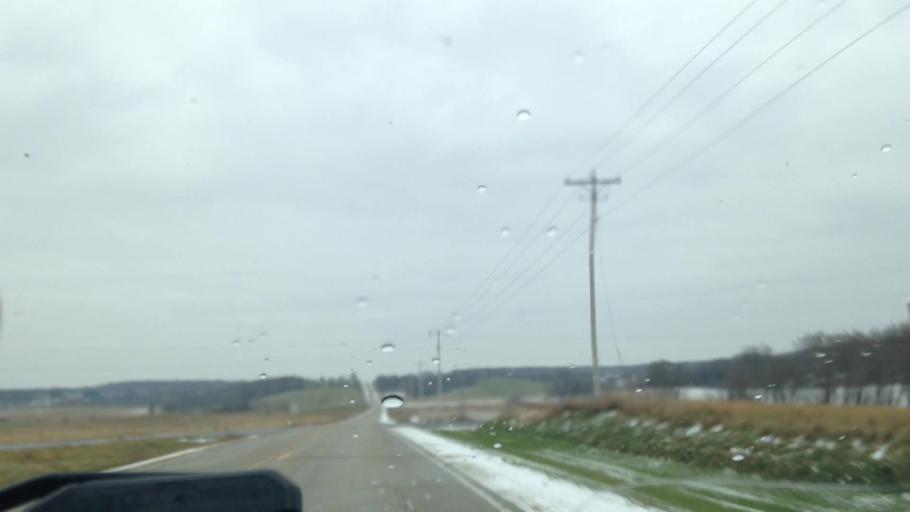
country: US
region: Wisconsin
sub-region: Dodge County
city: Mayville
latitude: 43.4720
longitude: -88.4995
